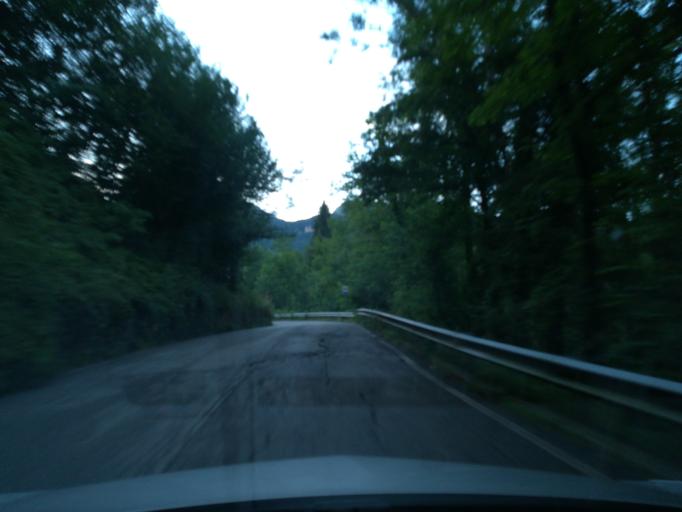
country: IT
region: Lombardy
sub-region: Provincia di Bergamo
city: Rota d'Imagna
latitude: 45.8237
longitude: 9.5080
